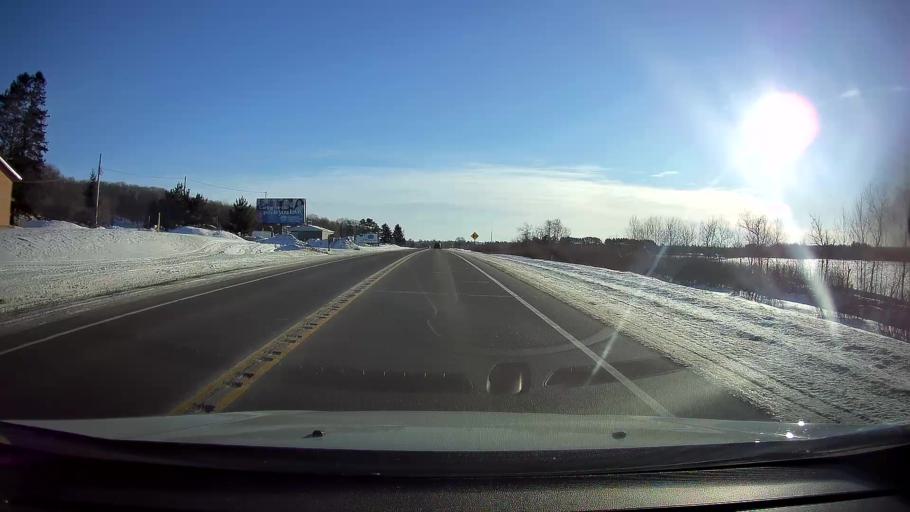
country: US
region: Wisconsin
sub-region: Sawyer County
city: Hayward
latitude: 45.9824
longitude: -91.5660
